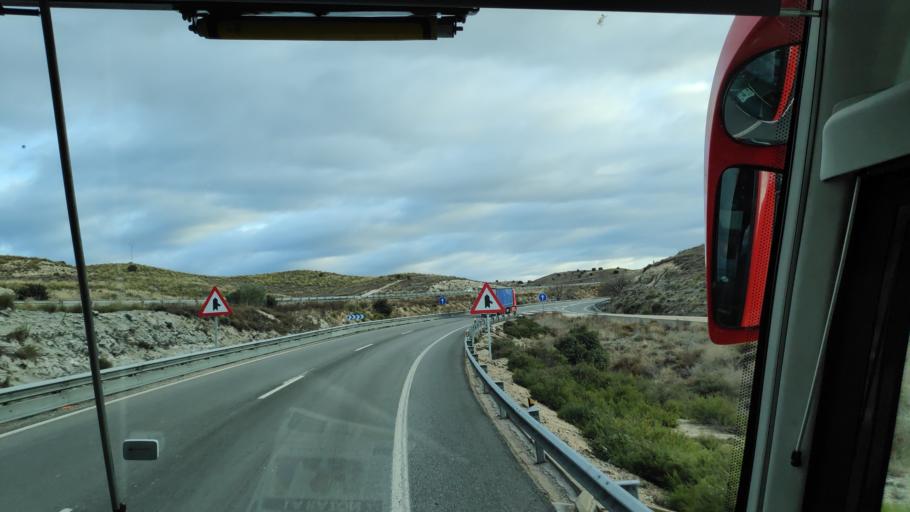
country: ES
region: Madrid
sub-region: Provincia de Madrid
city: Tielmes
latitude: 40.2071
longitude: -3.3155
